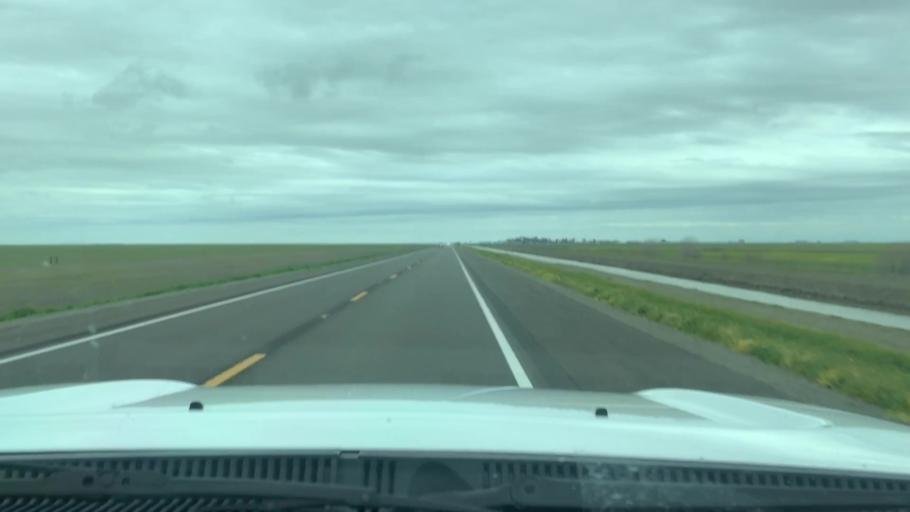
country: US
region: California
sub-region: Kings County
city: Kettleman City
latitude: 36.0983
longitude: -119.9077
